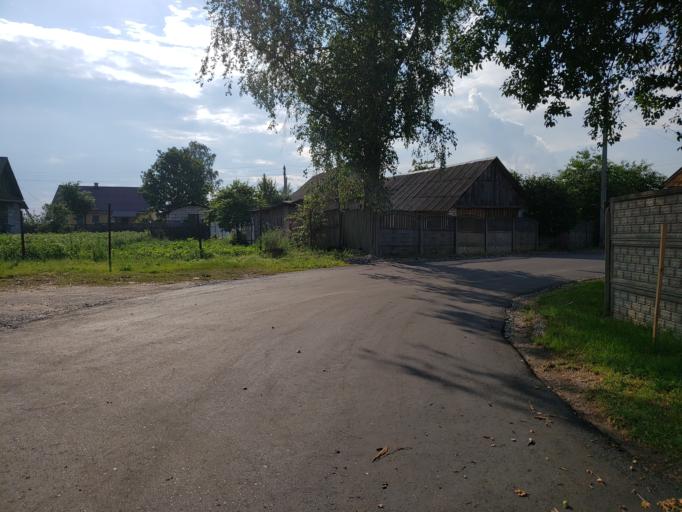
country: BY
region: Minsk
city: Chervyen'
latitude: 53.7151
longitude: 28.4045
